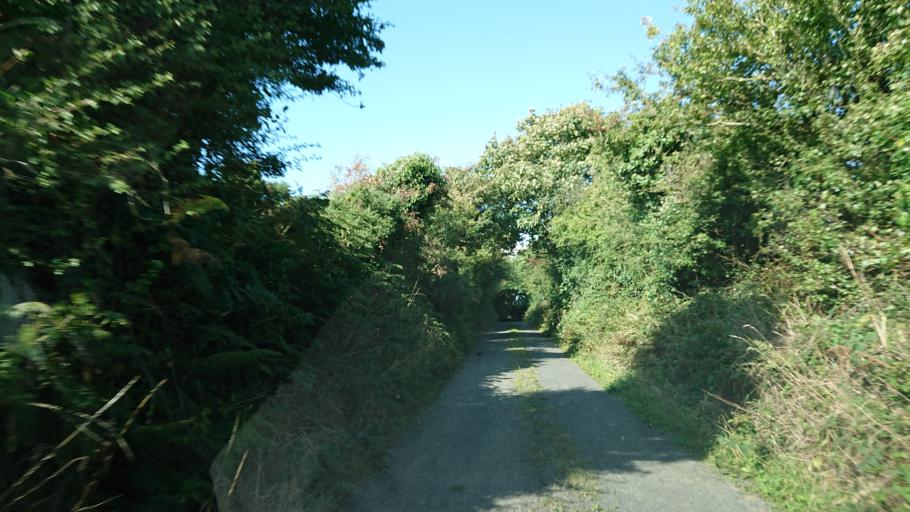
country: IE
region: Munster
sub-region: Waterford
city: Waterford
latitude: 52.2050
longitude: -7.0580
